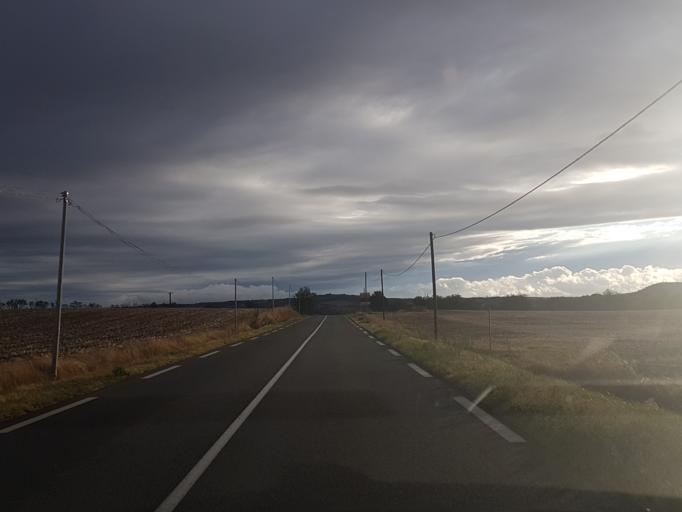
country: FR
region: Languedoc-Roussillon
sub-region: Departement de l'Aude
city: Bram
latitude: 43.2202
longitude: 2.0825
